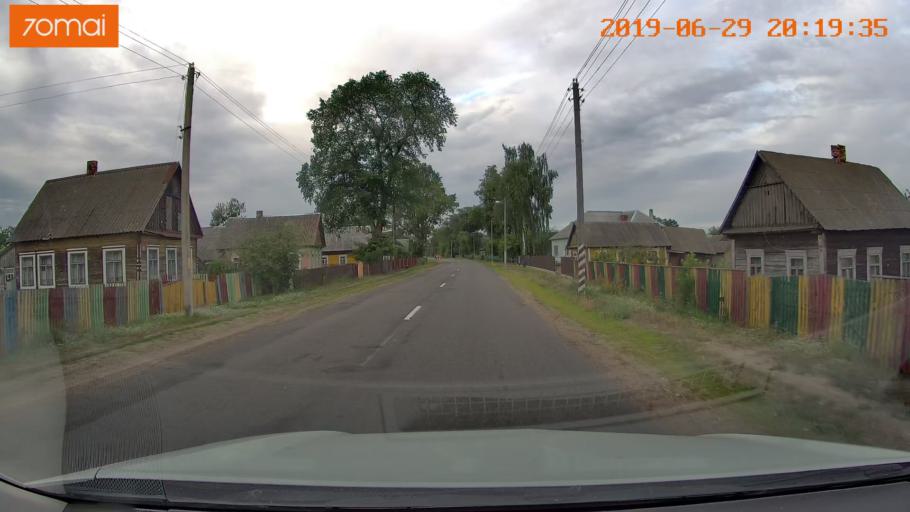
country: BY
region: Brest
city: Asnyezhytsy
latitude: 52.4027
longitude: 26.2451
